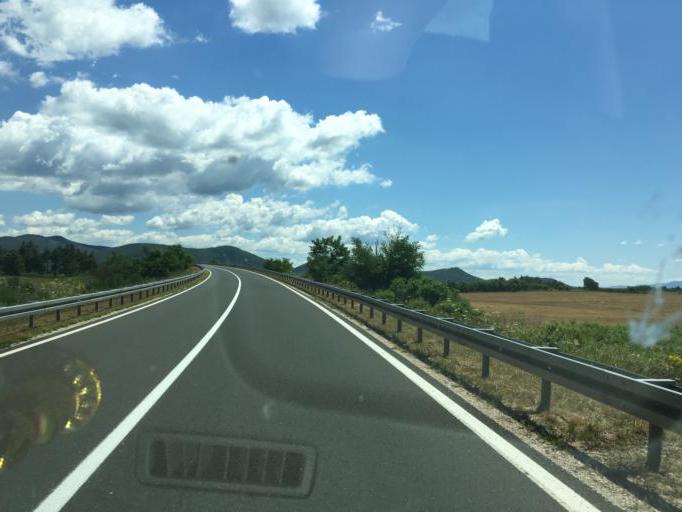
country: HR
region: Licko-Senjska
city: Gospic
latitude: 44.5751
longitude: 15.4075
